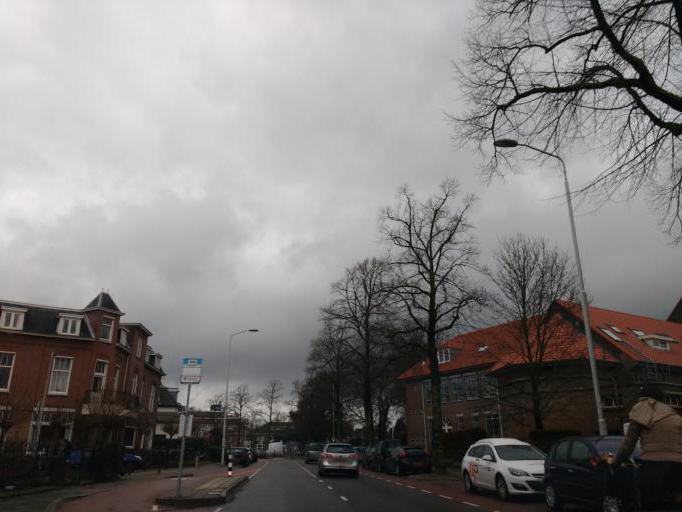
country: NL
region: Gelderland
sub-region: Gemeente Nijmegen
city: Nijmegen
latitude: 51.8367
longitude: 5.8852
